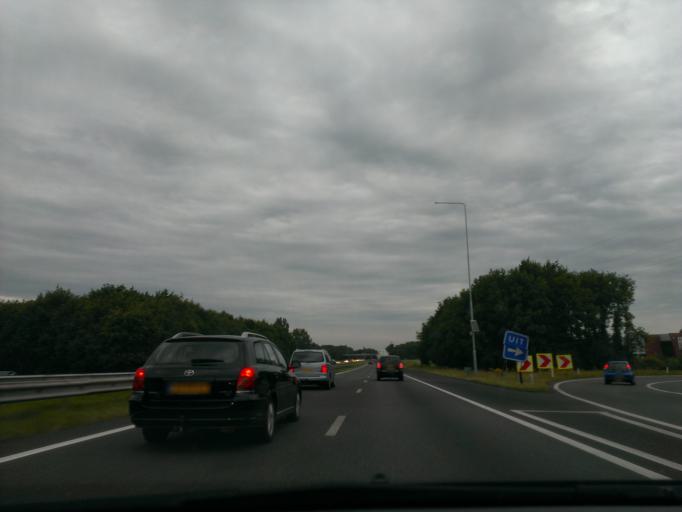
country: NL
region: Drenthe
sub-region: Gemeente Hoogeveen
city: Hoogeveen
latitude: 52.7208
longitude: 6.4647
